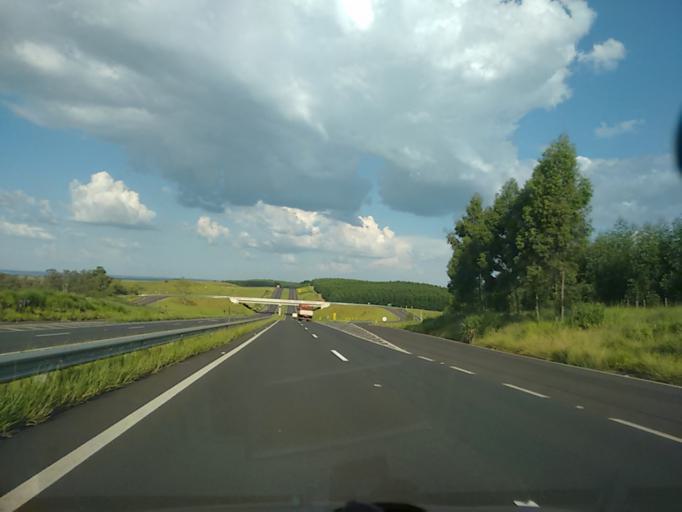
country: BR
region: Sao Paulo
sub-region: Duartina
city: Duartina
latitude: -22.3247
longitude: -49.4161
